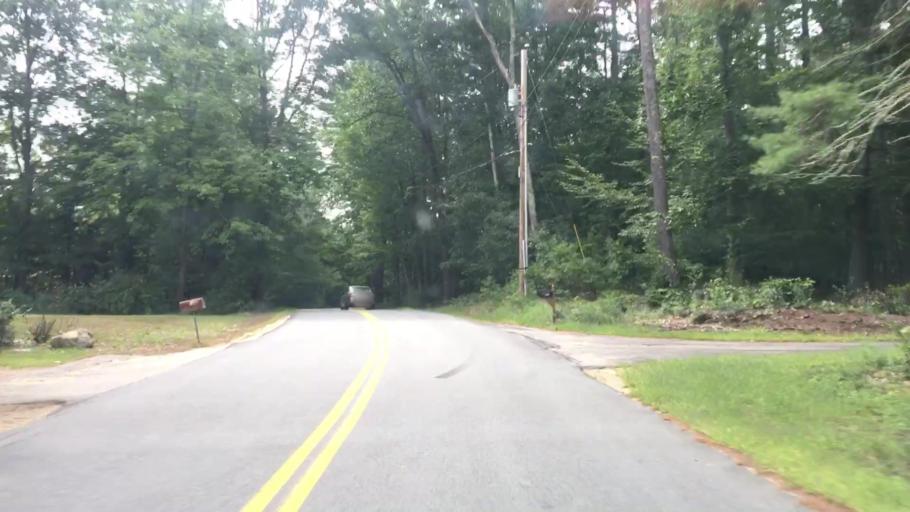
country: US
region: New Hampshire
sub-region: Strafford County
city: Barrington
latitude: 43.2006
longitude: -70.9869
